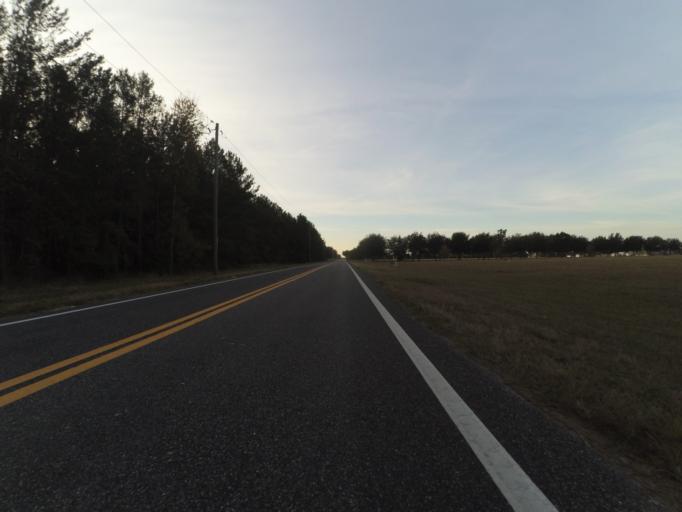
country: US
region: Florida
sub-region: Lake County
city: Umatilla
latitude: 28.9571
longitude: -81.6790
